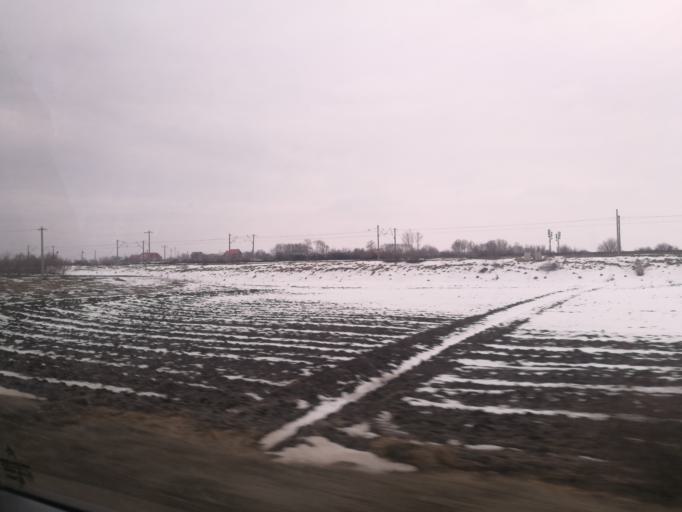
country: RO
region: Iasi
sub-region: Comuna Ruginoasa
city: Rediu
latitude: 47.2453
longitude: 26.8711
